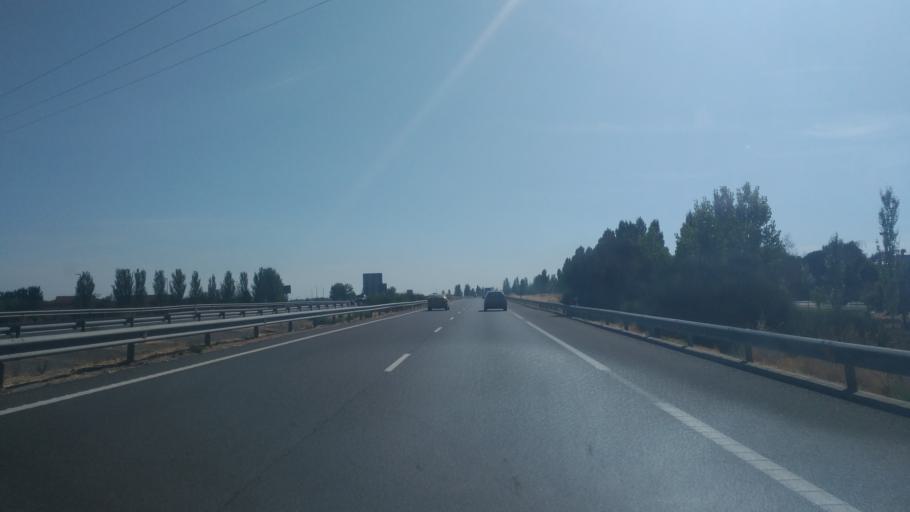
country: ES
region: Castille and Leon
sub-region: Provincia de Salamanca
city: Santa Marta de Tormes
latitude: 40.9445
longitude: -5.6301
